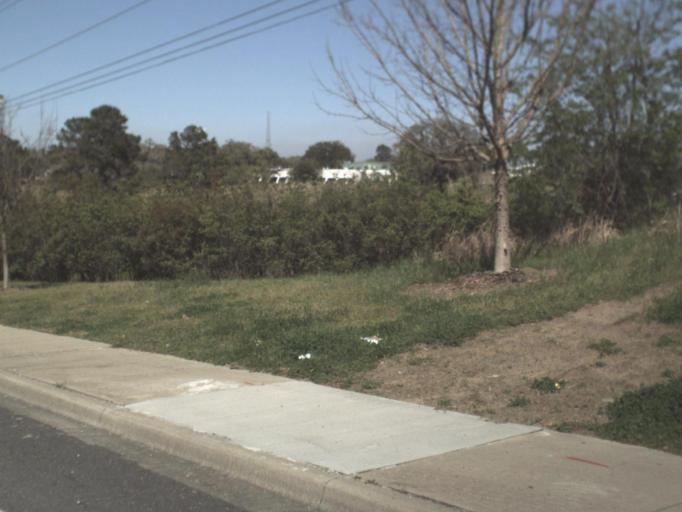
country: US
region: Florida
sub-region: Leon County
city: Tallahassee
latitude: 30.4334
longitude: -84.2265
